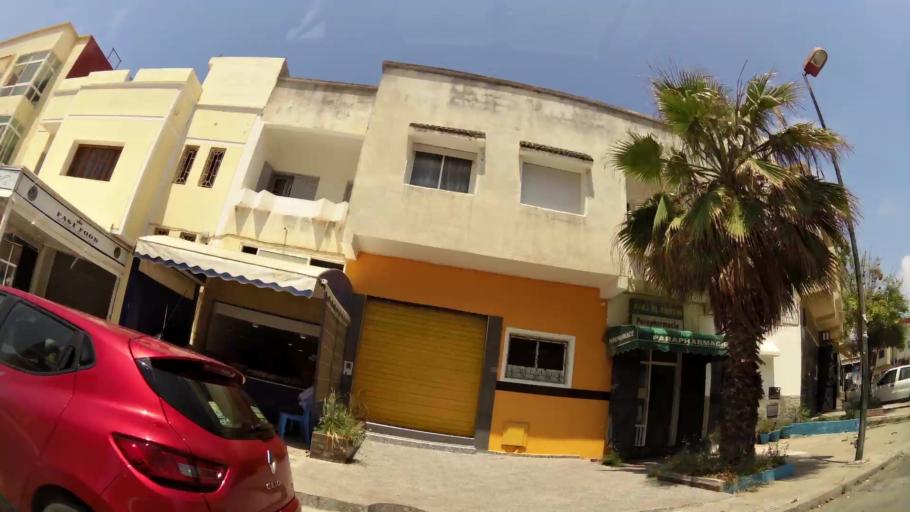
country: MA
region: Rabat-Sale-Zemmour-Zaer
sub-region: Skhirate-Temara
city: Temara
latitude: 33.9758
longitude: -6.8952
